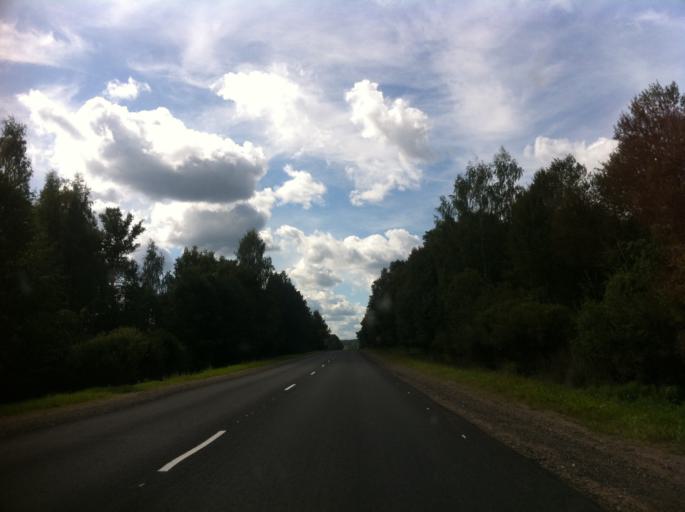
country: RU
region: Pskov
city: Izborsk
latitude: 57.7114
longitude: 27.8989
